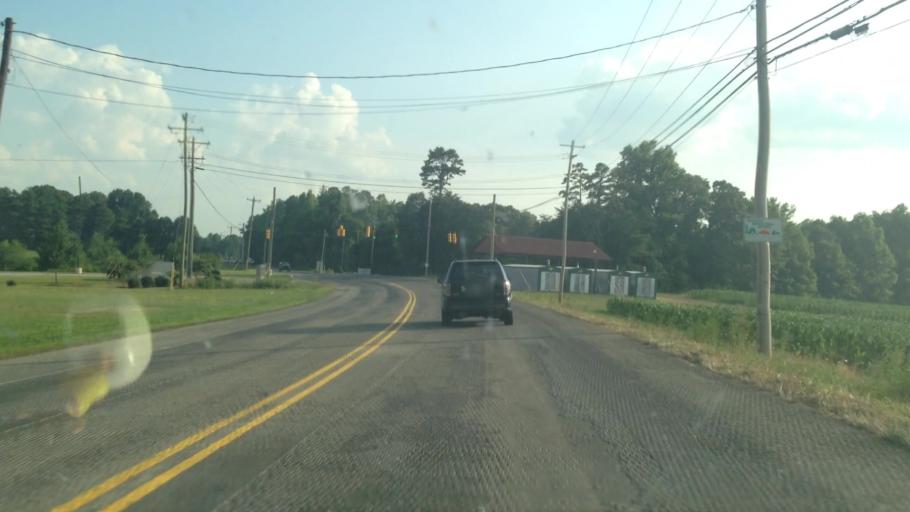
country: US
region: North Carolina
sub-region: Forsyth County
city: Kernersville
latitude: 36.0346
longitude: -80.0543
